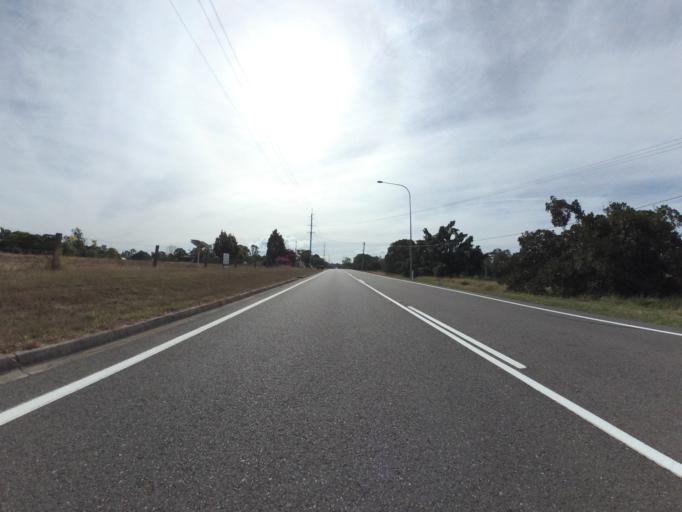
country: AU
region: Queensland
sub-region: Brisbane
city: Moggill
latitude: -27.5904
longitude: 152.8605
